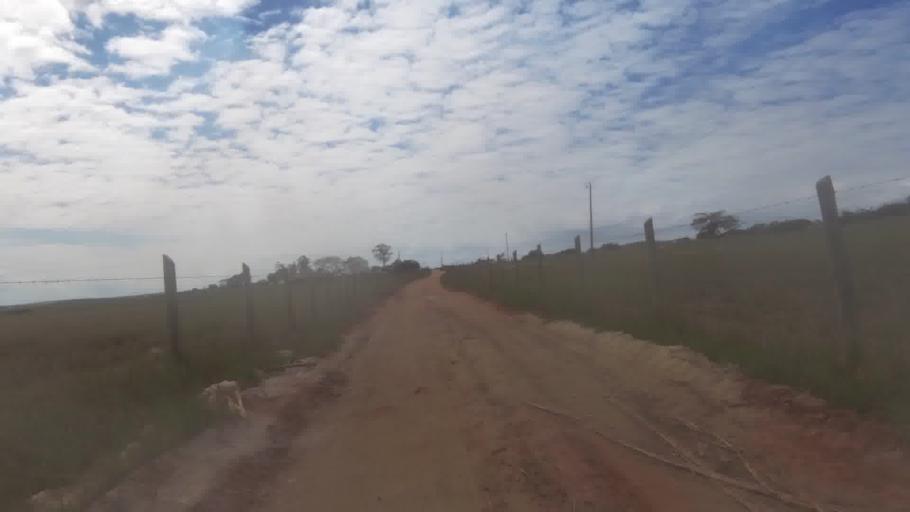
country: BR
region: Espirito Santo
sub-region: Marataizes
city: Marataizes
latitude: -21.2371
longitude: -40.9945
